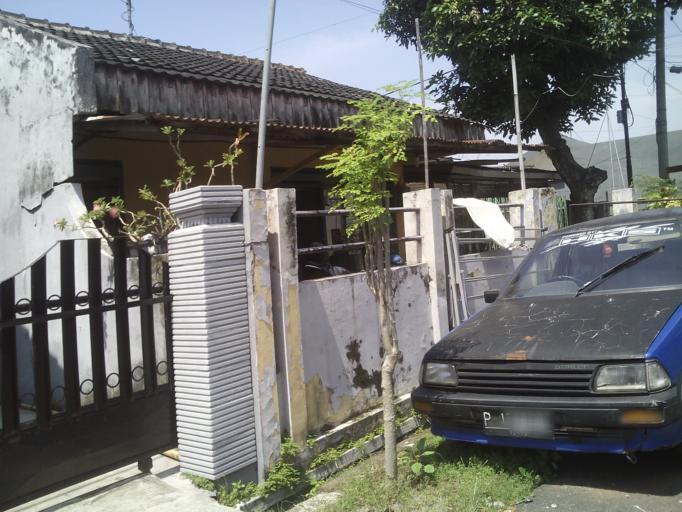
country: ID
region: East Java
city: Sumbersari Wetan
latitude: -8.1795
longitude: 113.7213
